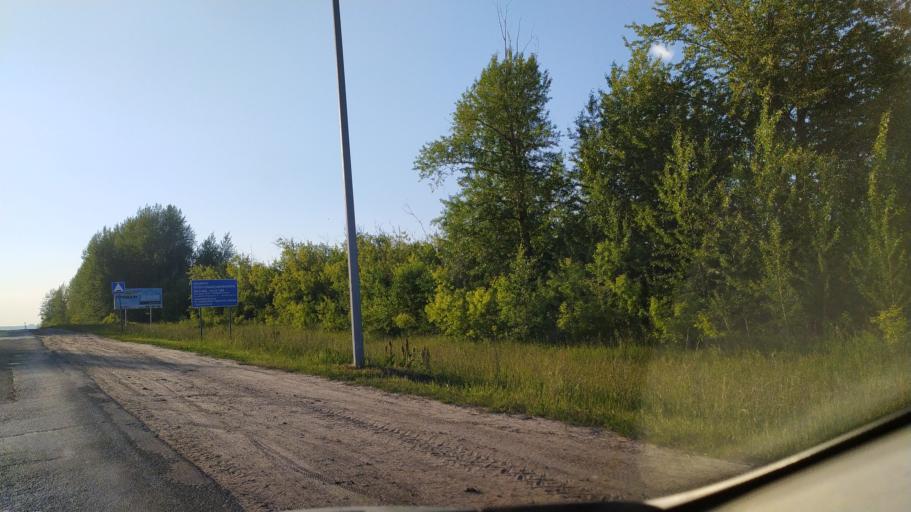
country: RU
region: Chuvashia
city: Kugesi
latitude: 56.0373
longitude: 47.3513
